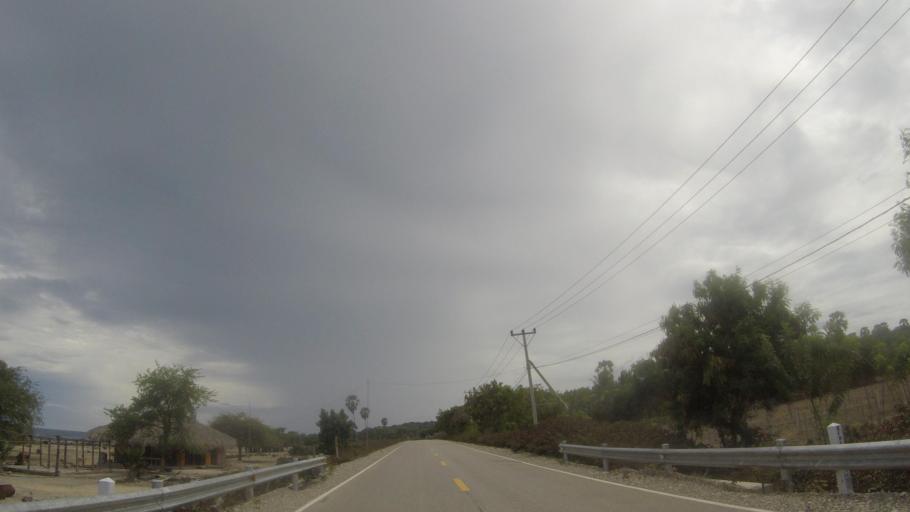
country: TL
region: Baucau
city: Baucau
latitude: -8.4296
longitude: 126.6859
